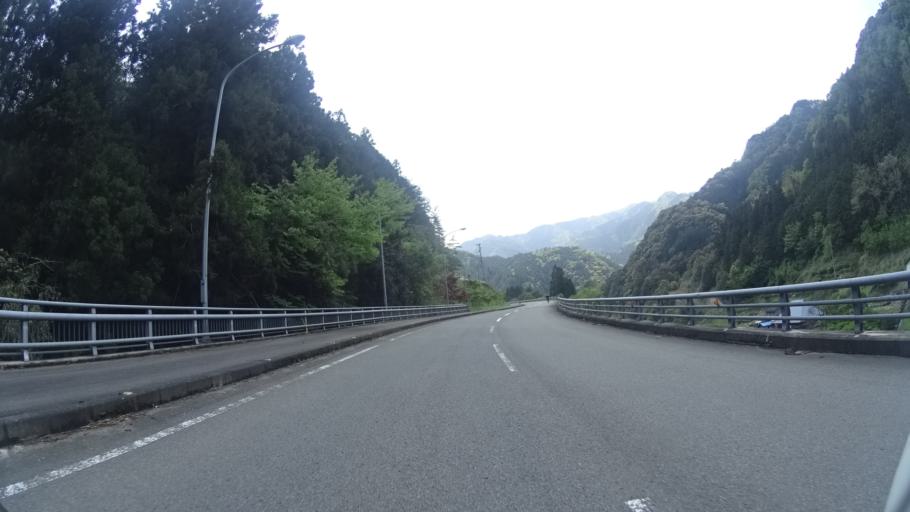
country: JP
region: Tokushima
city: Wakimachi
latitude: 33.9954
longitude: 134.0852
